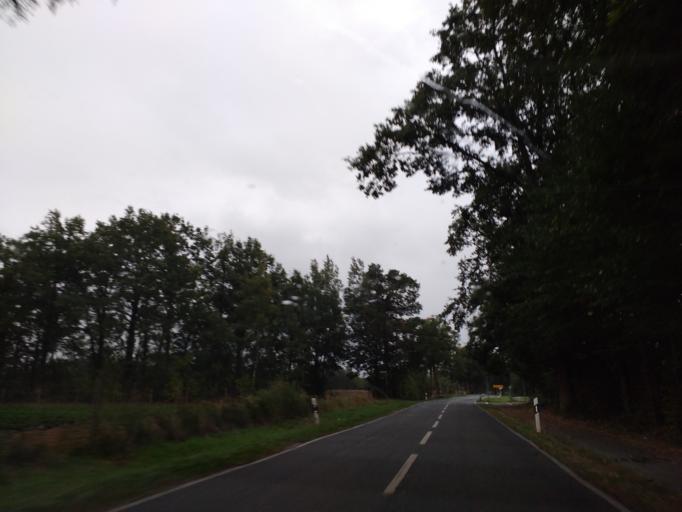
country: DE
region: North Rhine-Westphalia
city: Rietberg
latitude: 51.7305
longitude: 8.4437
